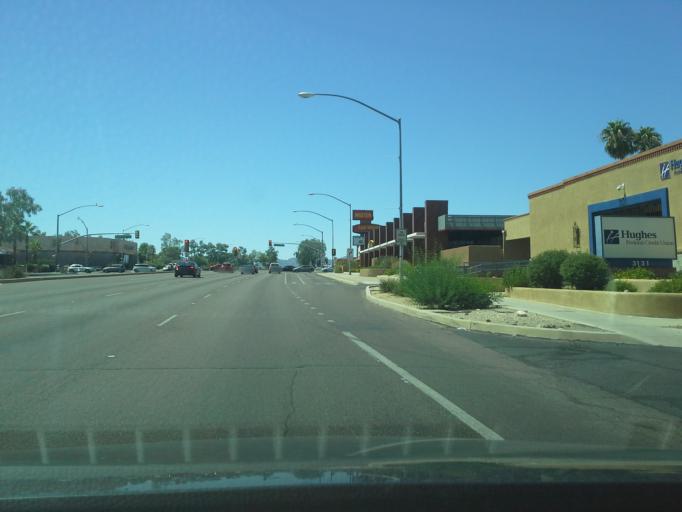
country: US
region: Arizona
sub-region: Pima County
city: Tucson
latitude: 32.2361
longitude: -110.9254
